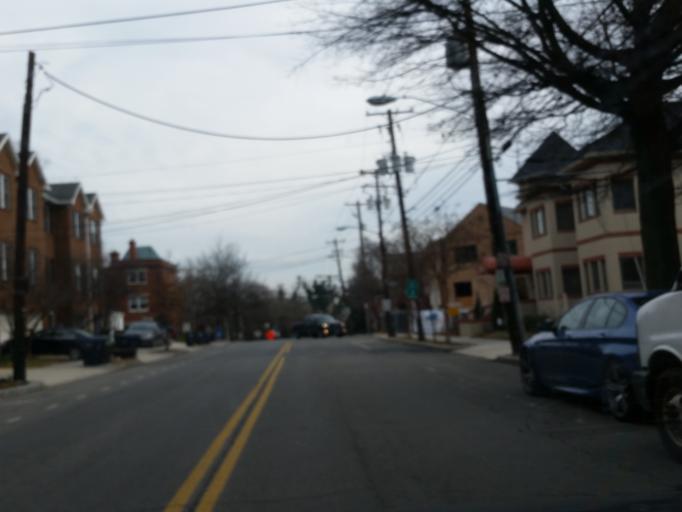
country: US
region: Virginia
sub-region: Arlington County
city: Arlington
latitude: 38.9074
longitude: -77.0827
